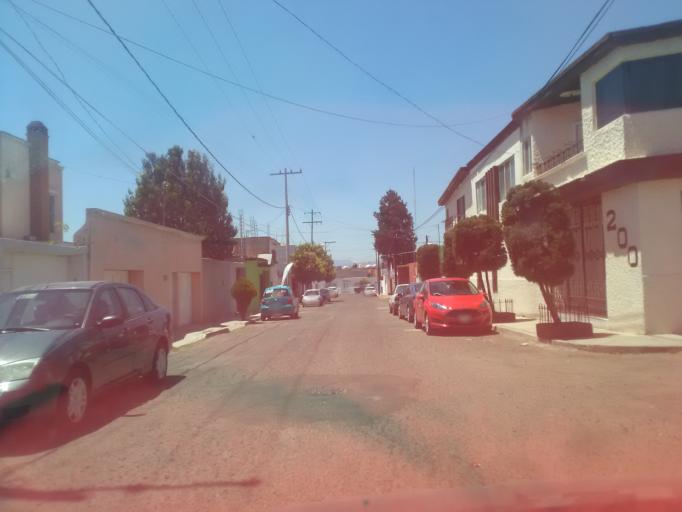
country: MX
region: Durango
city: Victoria de Durango
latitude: 24.0134
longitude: -104.6795
